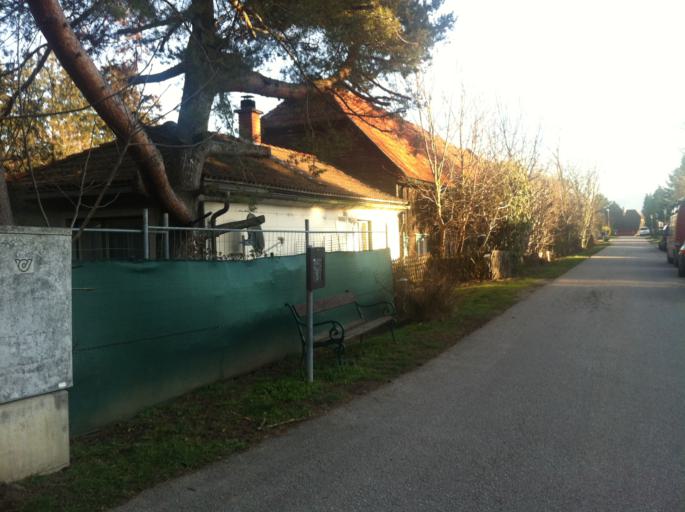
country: AT
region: Lower Austria
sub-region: Politischer Bezirk Wien-Umgebung
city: Gablitz
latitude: 48.2253
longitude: 16.1577
